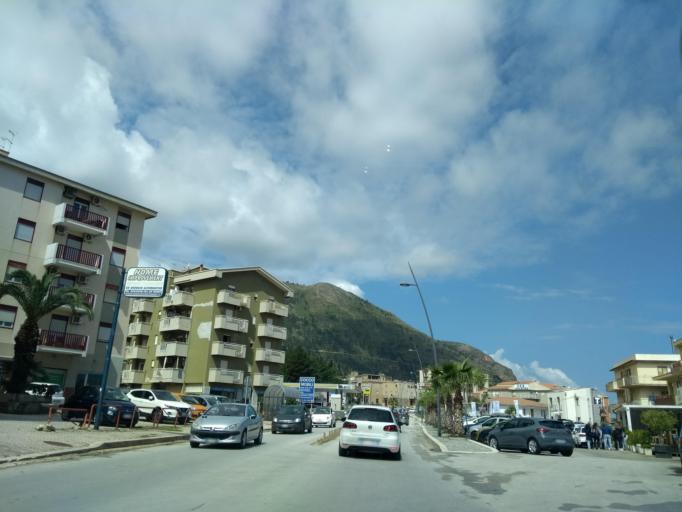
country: IT
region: Sicily
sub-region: Trapani
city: Castellammare del Golfo
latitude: 38.0162
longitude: 12.8904
